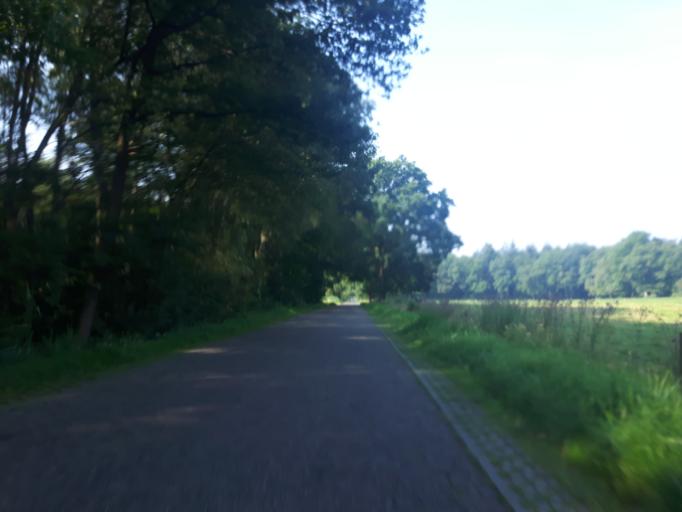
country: NL
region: Overijssel
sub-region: Gemeente Haaksbergen
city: Haaksbergen
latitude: 52.1890
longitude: 6.7803
